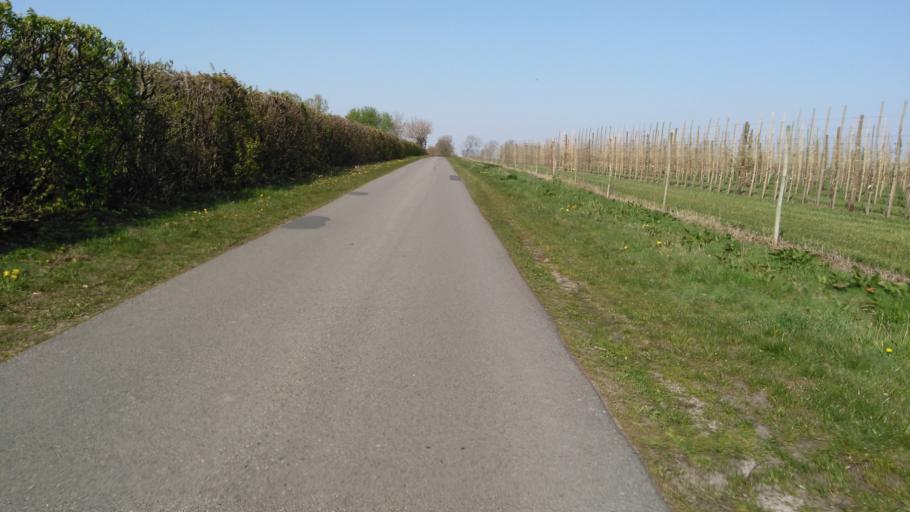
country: DE
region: Lower Saxony
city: Bliedersdorf
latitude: 53.4664
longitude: 9.5665
